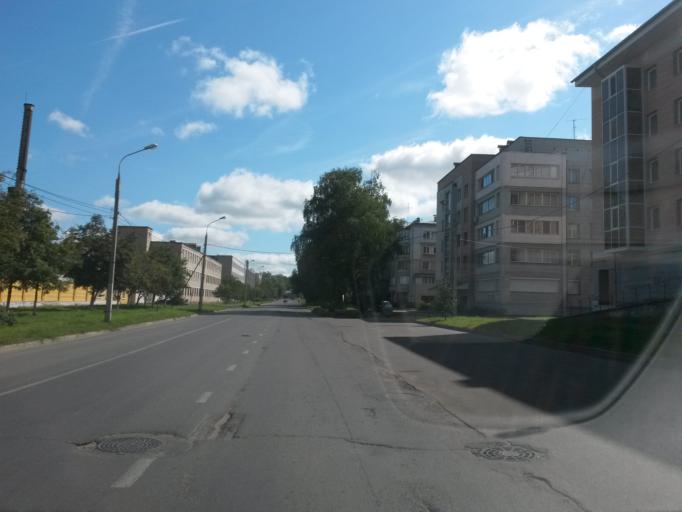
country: RU
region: Jaroslavl
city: Yaroslavl
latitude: 57.6061
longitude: 39.8727
